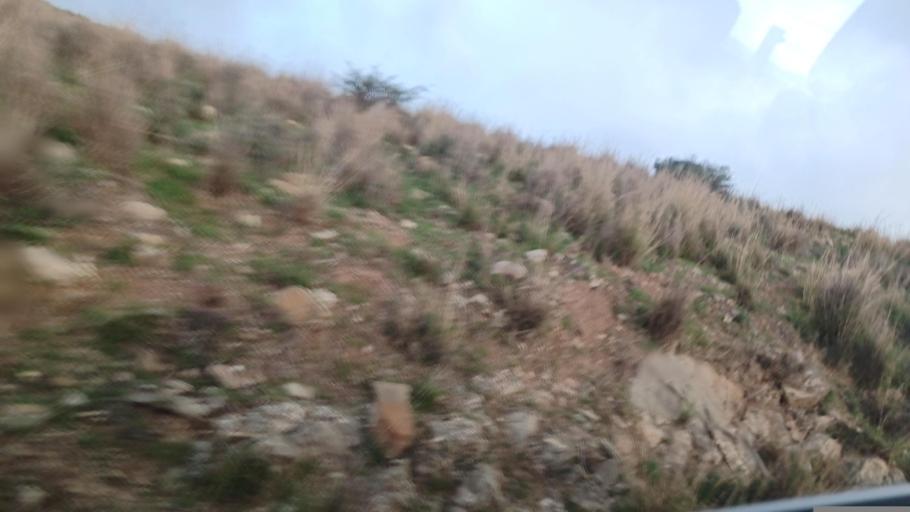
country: CY
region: Pafos
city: Mesogi
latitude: 34.7850
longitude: 32.5147
